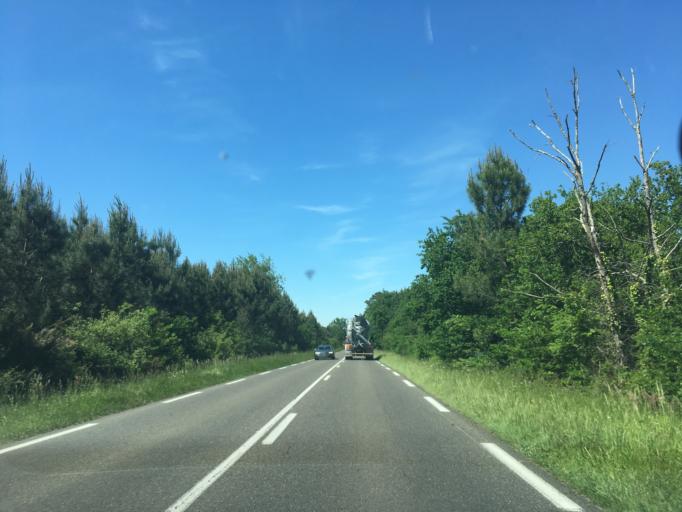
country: FR
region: Aquitaine
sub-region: Departement de la Gironde
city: Listrac-Medoc
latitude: 45.0932
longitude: -0.7991
